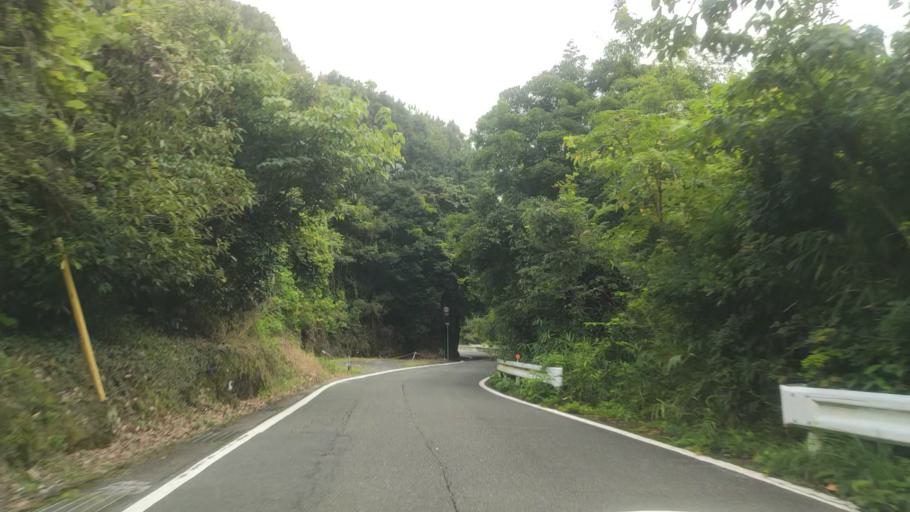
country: JP
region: Wakayama
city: Hashimoto
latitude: 34.2807
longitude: 135.5627
